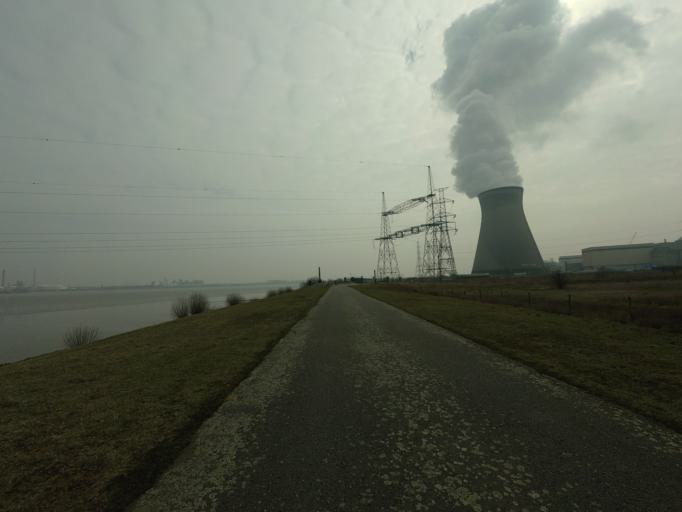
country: NL
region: North Brabant
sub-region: Gemeente Woensdrecht
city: Woensdrecht
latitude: 51.3324
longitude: 4.2588
